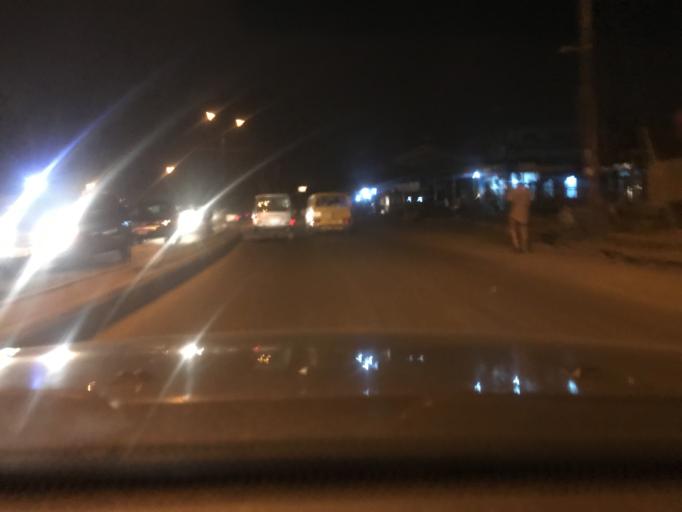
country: NG
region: Lagos
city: Agege
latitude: 6.6110
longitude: 3.2954
